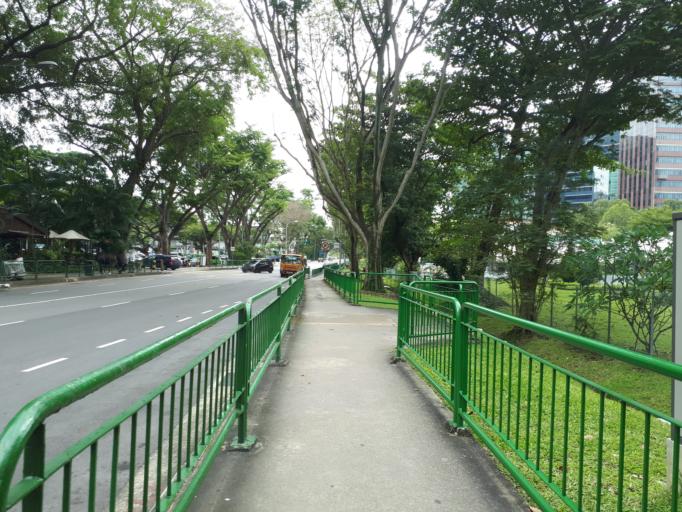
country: SG
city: Singapore
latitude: 1.3122
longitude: 103.8390
